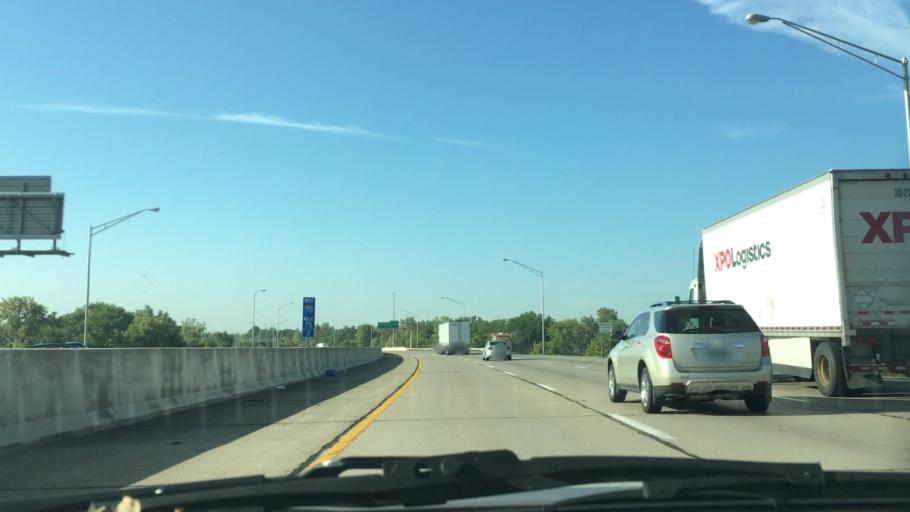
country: US
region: Indiana
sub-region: Marion County
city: Speedway
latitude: 39.7452
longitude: -86.2375
